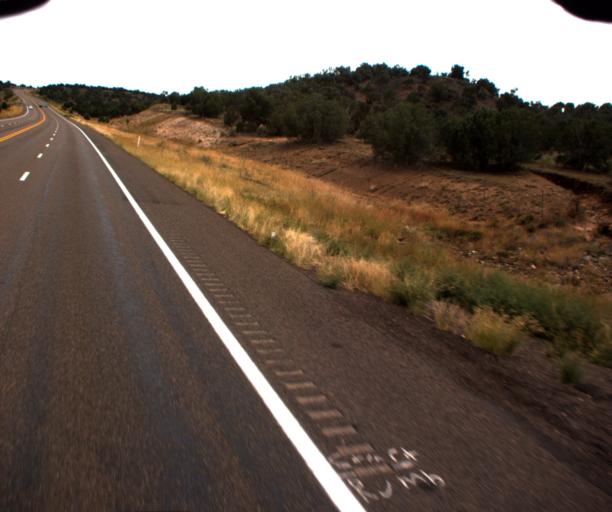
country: US
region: Arizona
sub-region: Navajo County
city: White Mountain Lake
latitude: 34.3817
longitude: -110.0586
